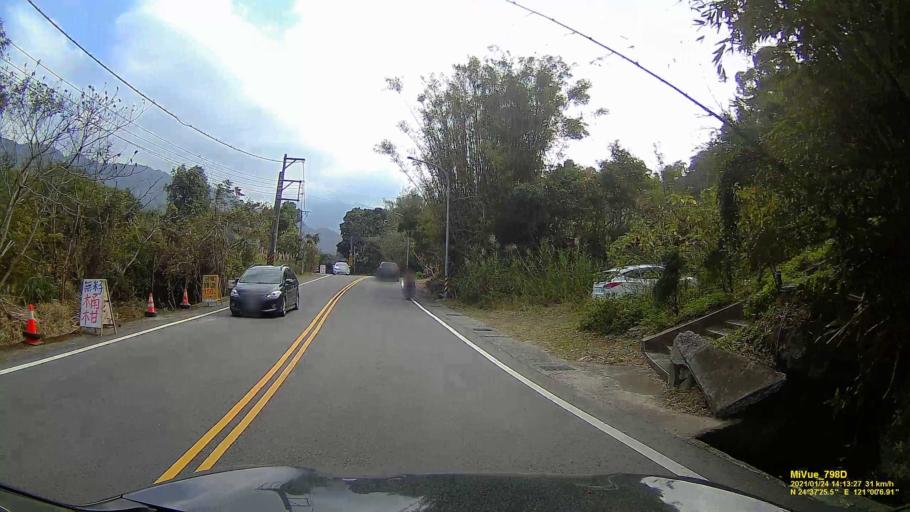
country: TW
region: Taiwan
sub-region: Hsinchu
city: Hsinchu
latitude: 24.6235
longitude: 121.0020
